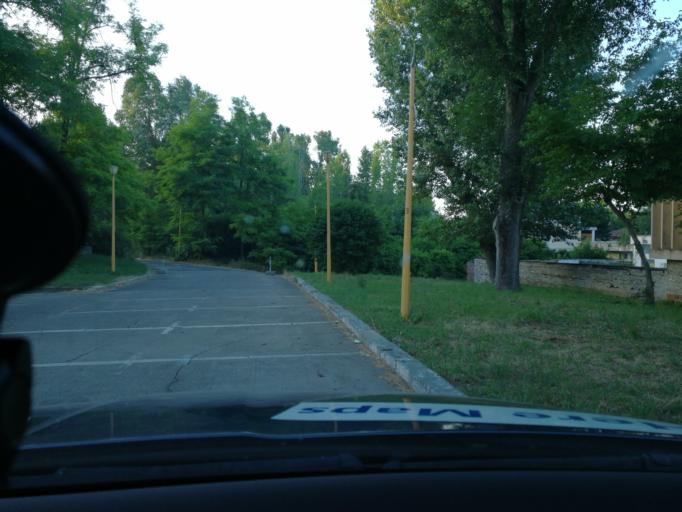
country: RO
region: Constanta
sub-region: Comuna Douazeci si Trei August
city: Douazeci si Trei August
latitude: 43.8693
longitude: 28.5978
